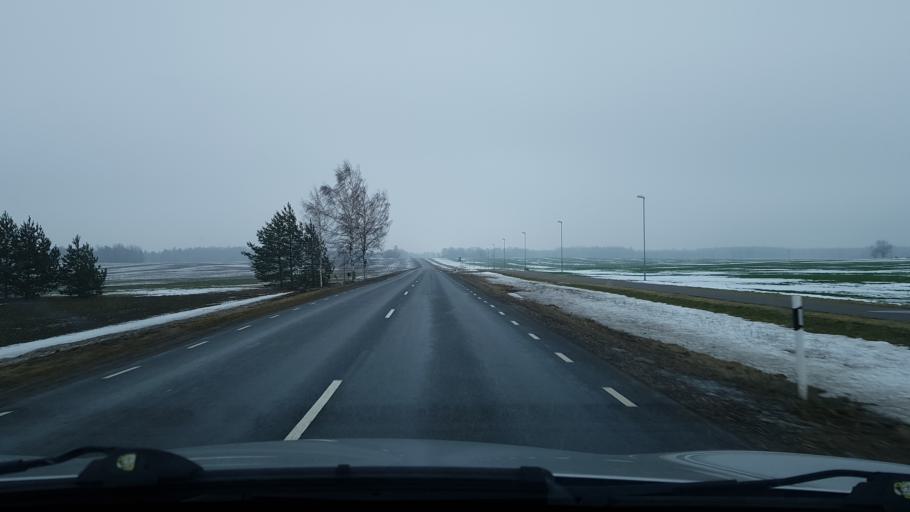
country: EE
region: Valgamaa
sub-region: Torva linn
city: Torva
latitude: 58.2197
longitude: 25.9015
